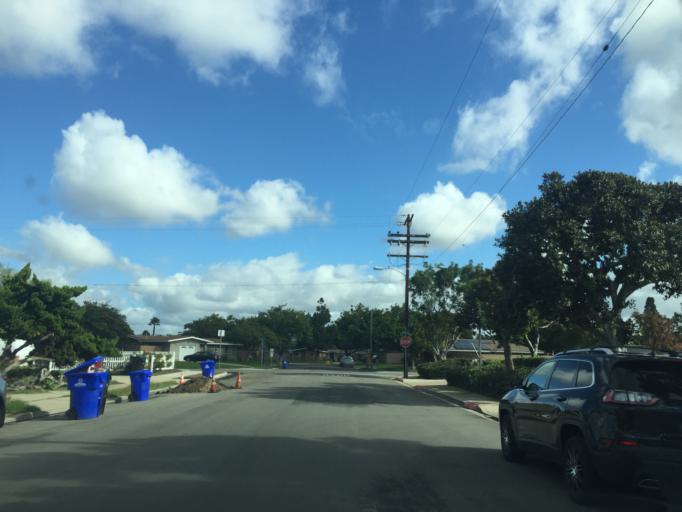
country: US
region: California
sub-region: San Diego County
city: La Jolla
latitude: 32.7973
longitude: -117.2290
